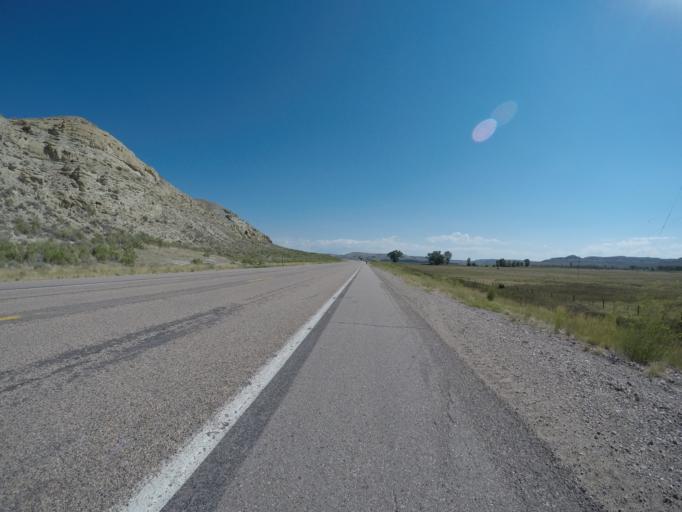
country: US
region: Wyoming
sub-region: Sublette County
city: Marbleton
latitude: 42.1844
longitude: -110.1825
